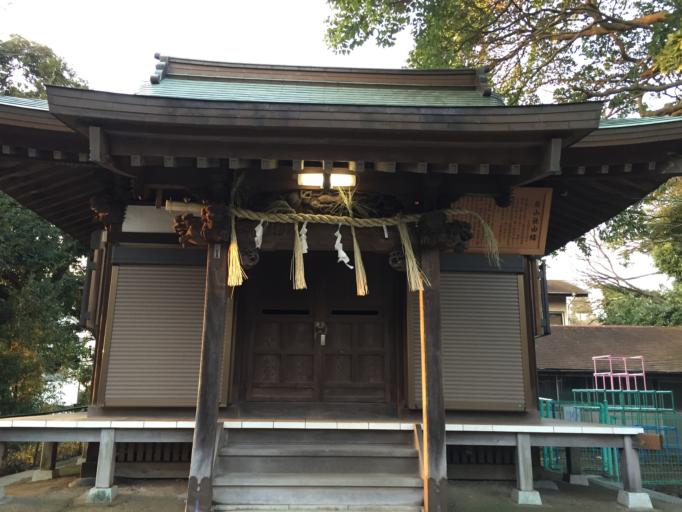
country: JP
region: Kanagawa
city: Yokohama
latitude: 35.4144
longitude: 139.5882
